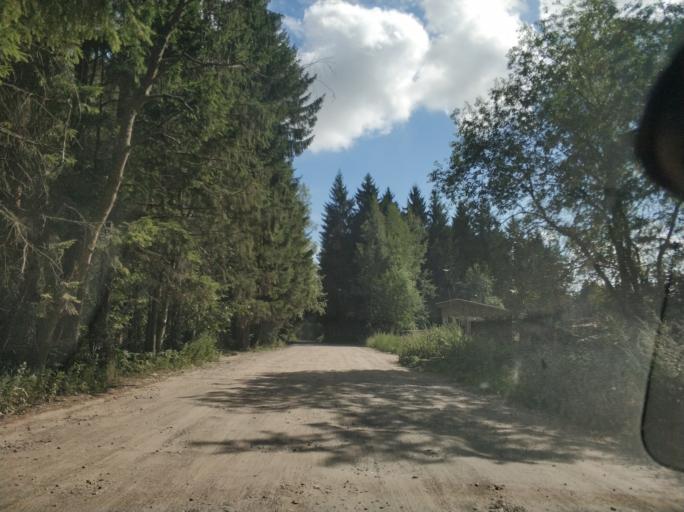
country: RU
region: Leningrad
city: Vsevolozhsk
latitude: 60.0218
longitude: 30.6117
